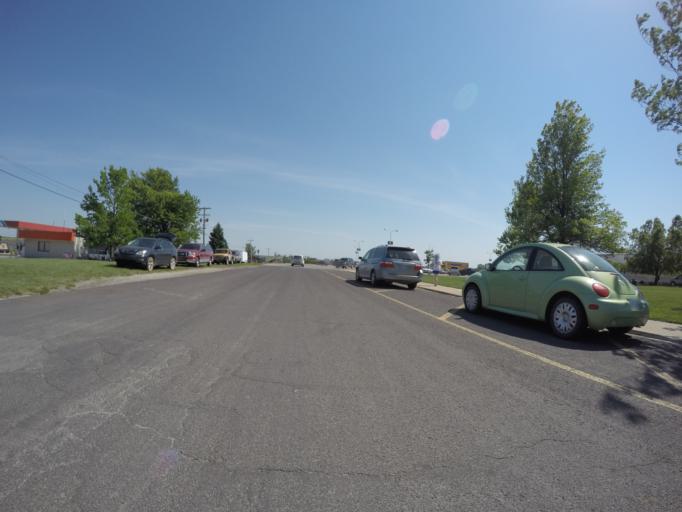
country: US
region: Kansas
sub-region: Nemaha County
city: Sabetha
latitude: 39.8945
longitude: -95.7892
